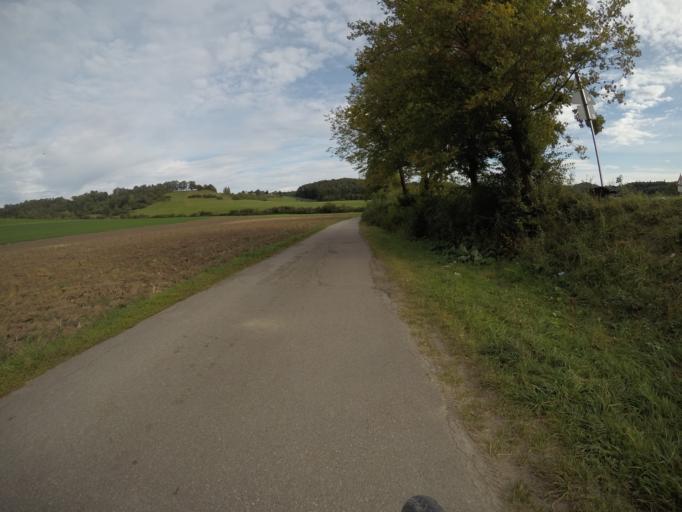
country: DE
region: Baden-Wuerttemberg
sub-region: Regierungsbezirk Stuttgart
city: Leonberg
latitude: 48.7772
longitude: 9.0327
